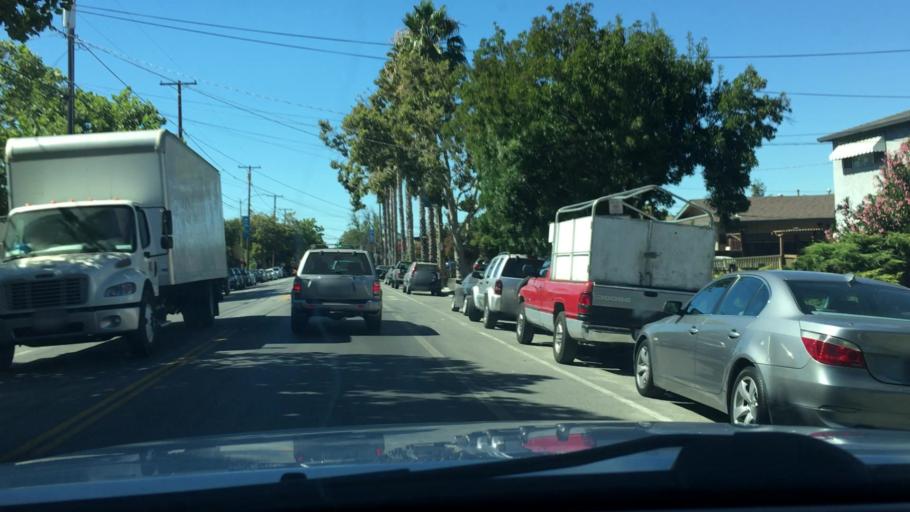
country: US
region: California
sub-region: Santa Clara County
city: San Jose
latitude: 37.3240
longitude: -121.8729
